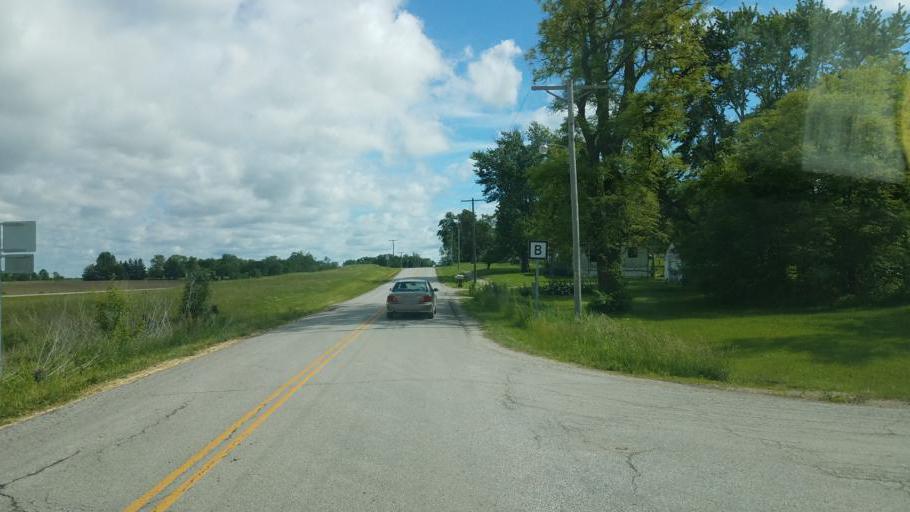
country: US
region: Missouri
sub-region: Mercer County
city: Princeton
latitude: 40.3293
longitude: -93.7971
